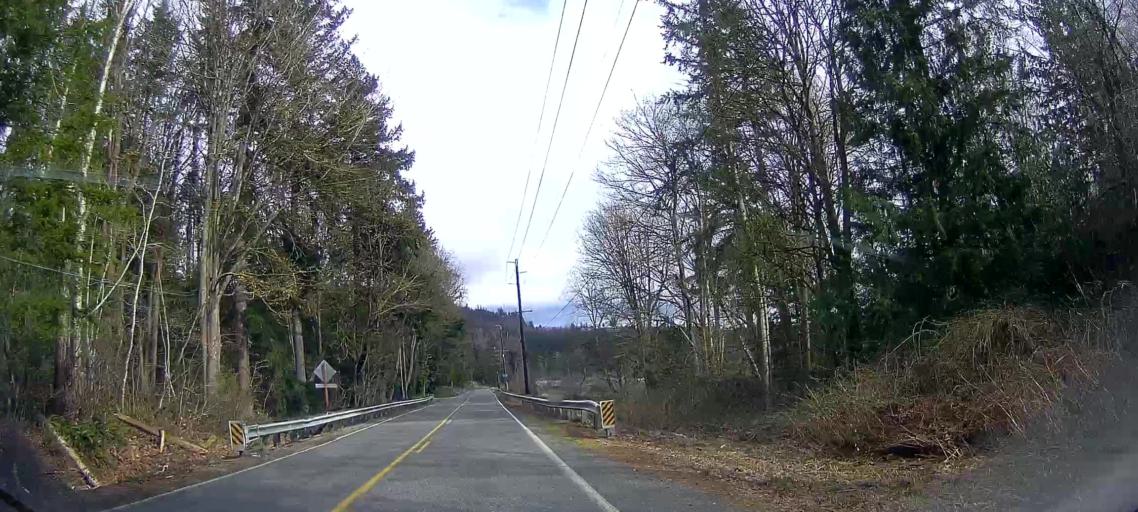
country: US
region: Washington
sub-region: Skagit County
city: Burlington
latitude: 48.5334
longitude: -122.3028
